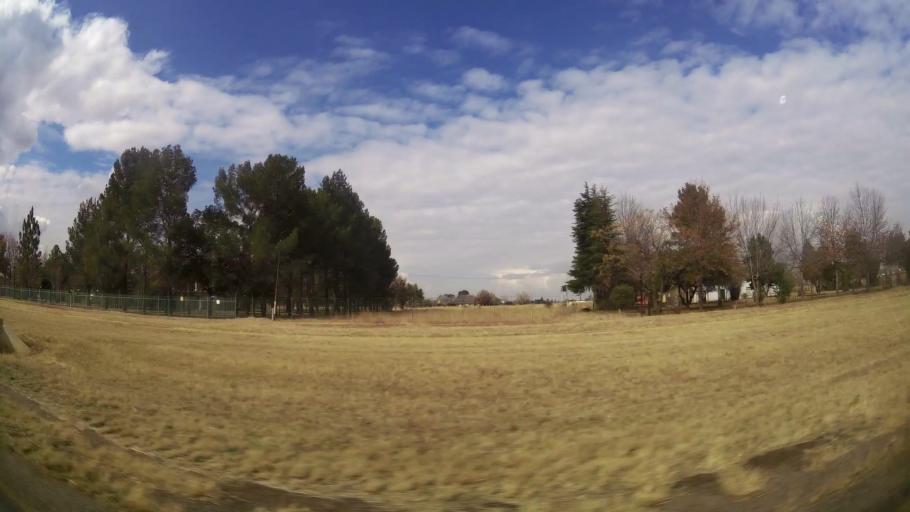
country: ZA
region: Gauteng
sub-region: Sedibeng District Municipality
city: Meyerton
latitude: -26.6435
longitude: 28.0356
